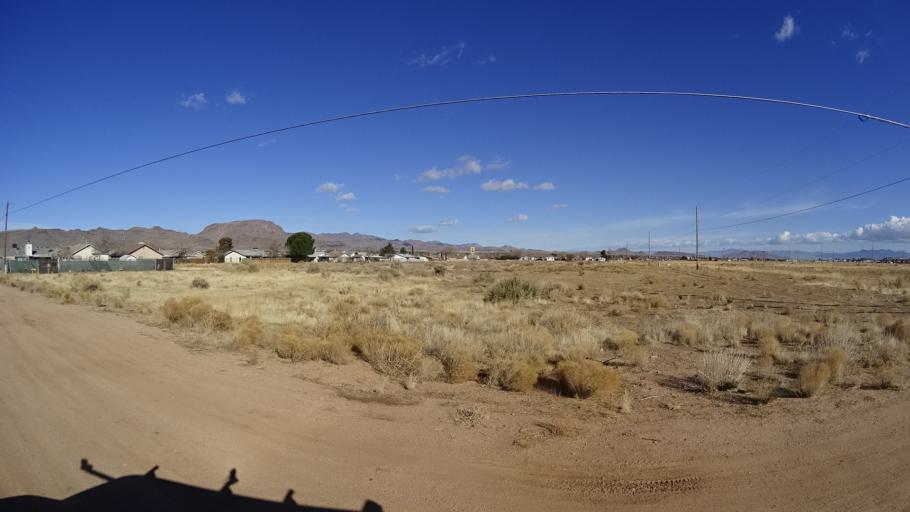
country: US
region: Arizona
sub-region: Mohave County
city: New Kingman-Butler
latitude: 35.2283
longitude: -114.0169
